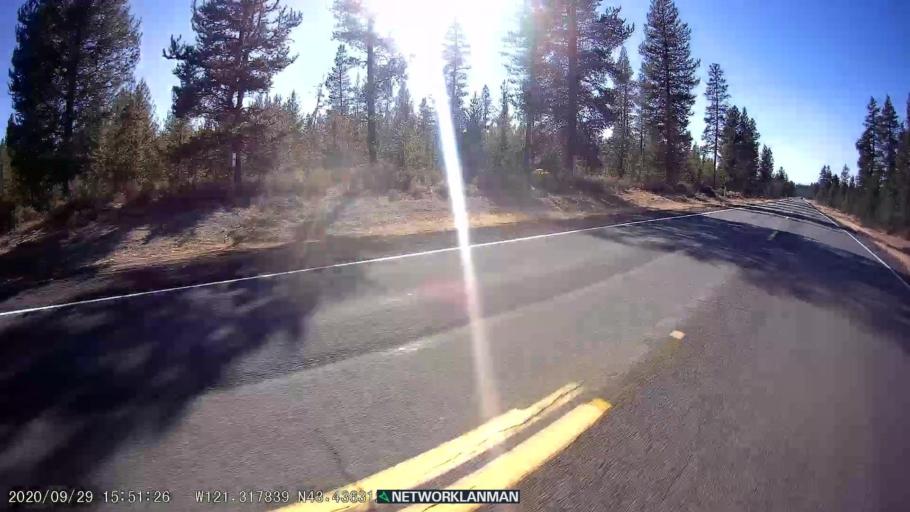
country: US
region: Oregon
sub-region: Deschutes County
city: La Pine
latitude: 43.4362
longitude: -121.3178
